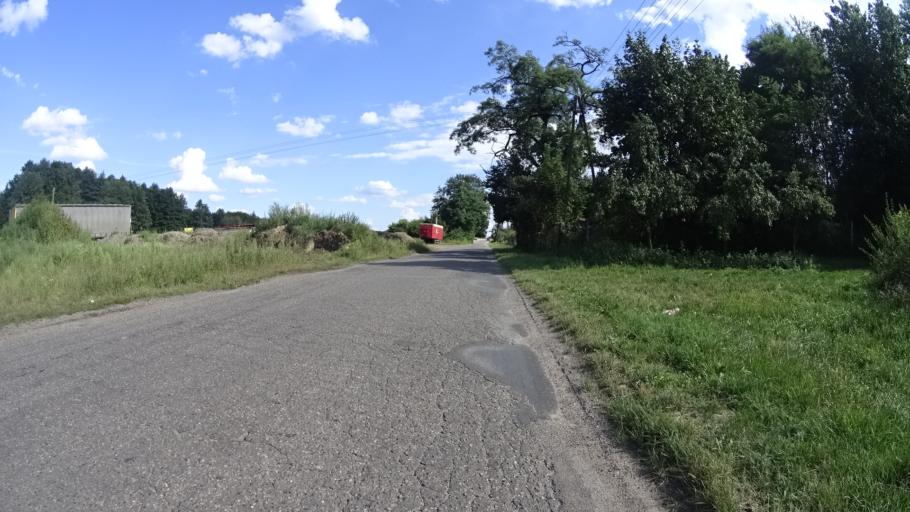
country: PL
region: Masovian Voivodeship
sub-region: Powiat grojecki
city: Mogielnica
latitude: 51.7010
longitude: 20.7105
